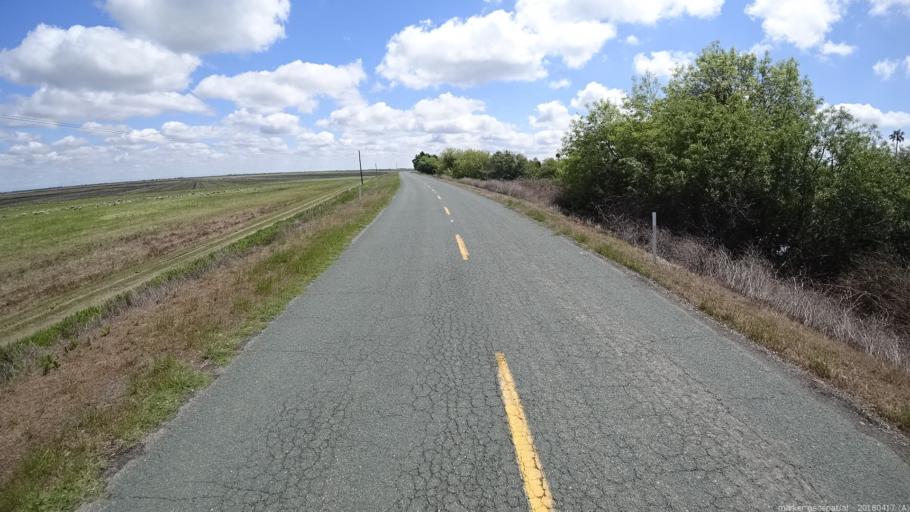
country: US
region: California
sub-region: Solano County
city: Rio Vista
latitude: 38.1520
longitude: -121.5897
